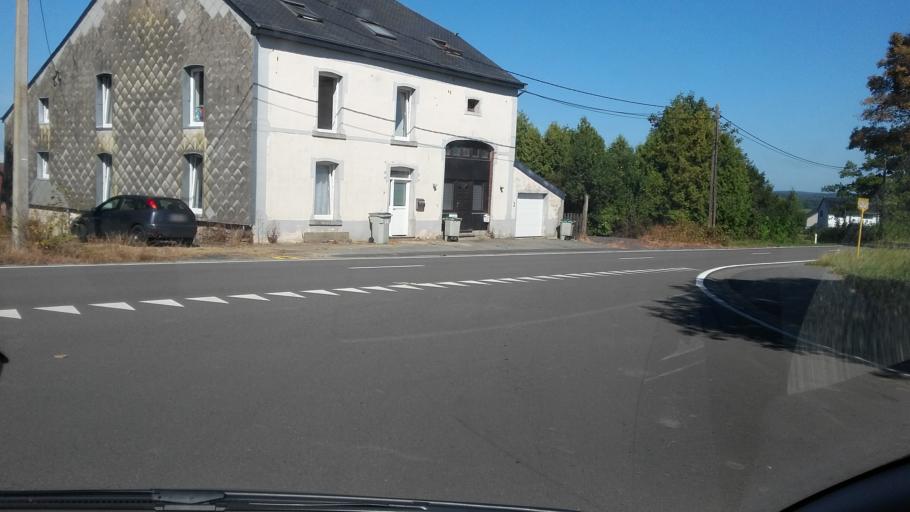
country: BE
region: Wallonia
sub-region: Province du Luxembourg
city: Neufchateau
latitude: 49.8167
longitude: 5.4156
